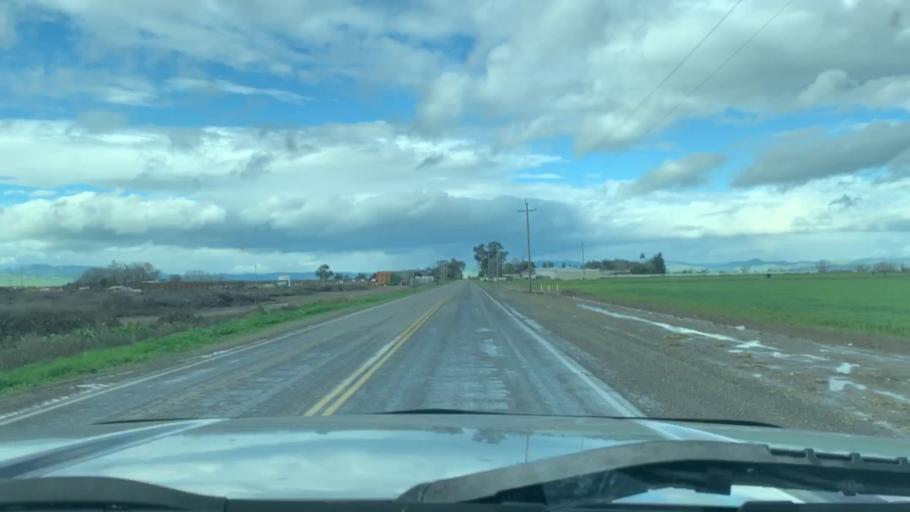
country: US
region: California
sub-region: Merced County
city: Los Banos
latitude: 37.1000
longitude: -120.8737
